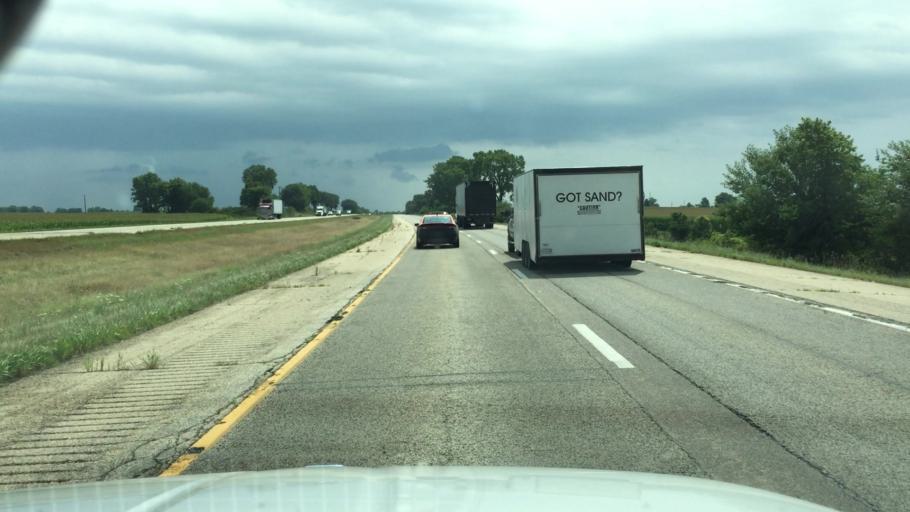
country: US
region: Illinois
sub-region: Peoria County
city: Elmwood
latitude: 40.8184
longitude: -89.8557
